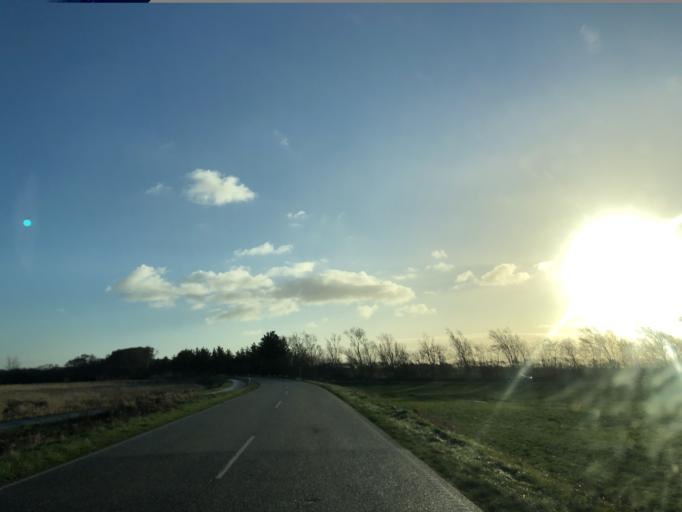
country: DK
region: Central Jutland
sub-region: Holstebro Kommune
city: Ulfborg
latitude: 56.2015
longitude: 8.2652
